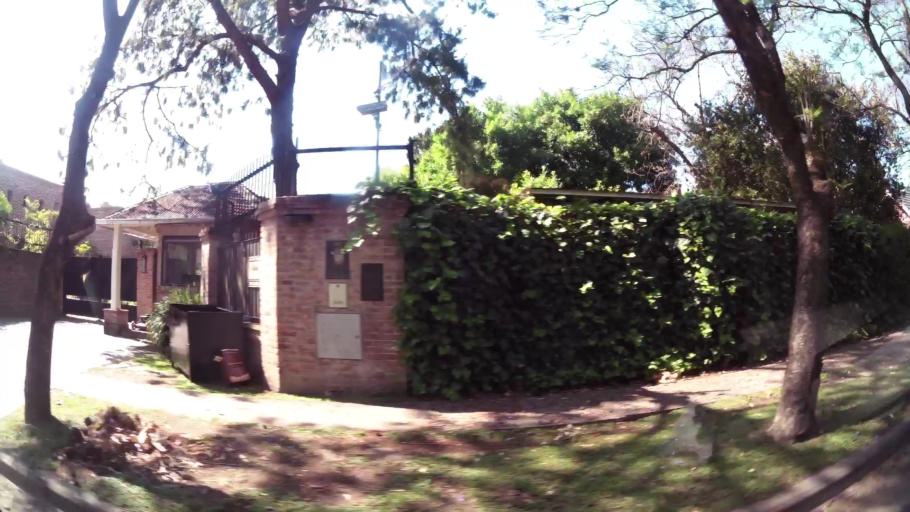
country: AR
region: Buenos Aires
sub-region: Partido de Tigre
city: Tigre
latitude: -34.4803
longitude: -58.5668
